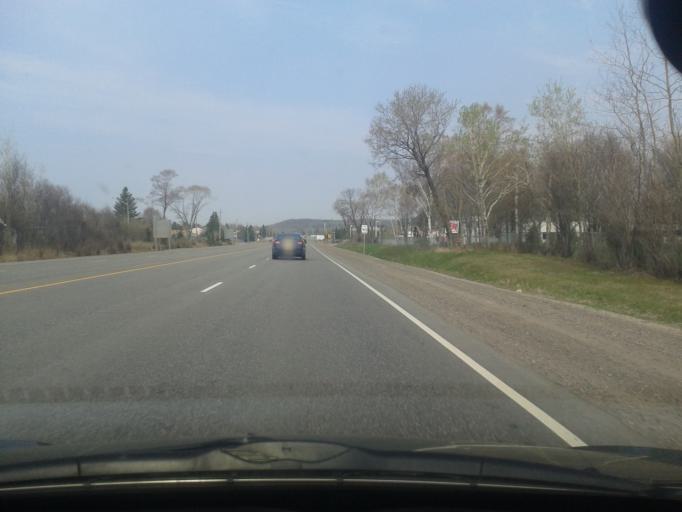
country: CA
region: Ontario
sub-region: Nipissing District
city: North Bay
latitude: 46.3306
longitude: -79.4751
